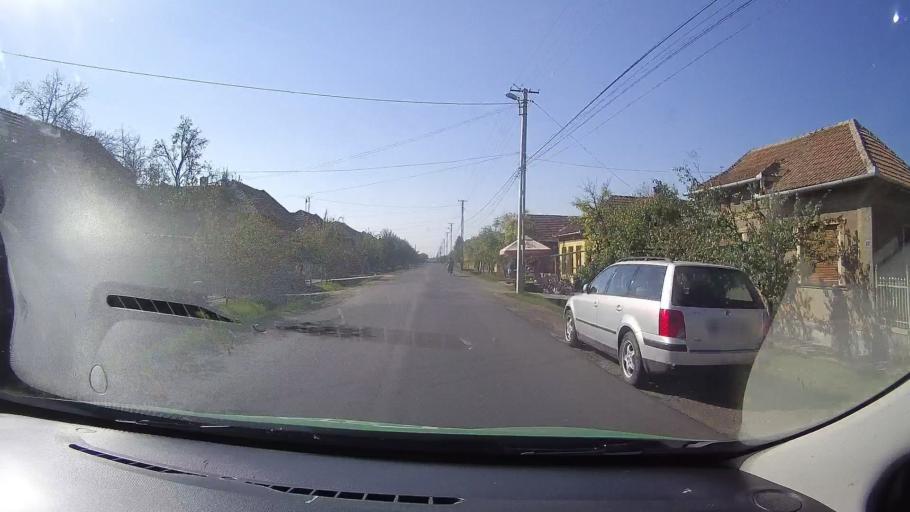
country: RO
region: Satu Mare
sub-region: Comuna Capleni
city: Capleni
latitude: 47.7031
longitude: 22.4943
